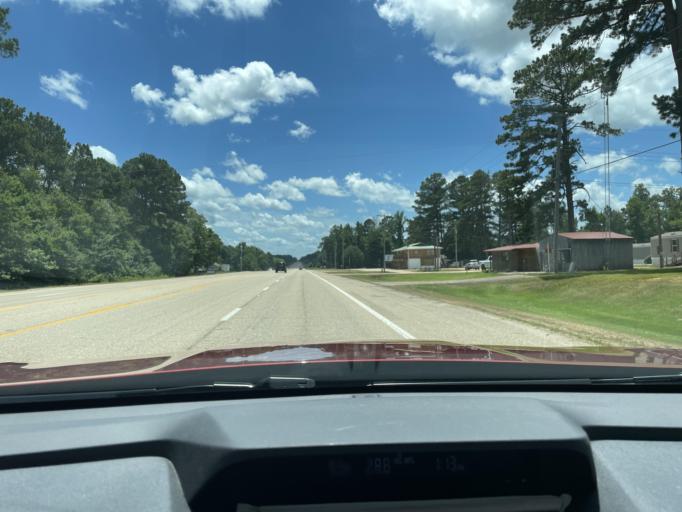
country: US
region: Arkansas
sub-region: Drew County
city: Monticello
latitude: 33.6775
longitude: -91.8049
